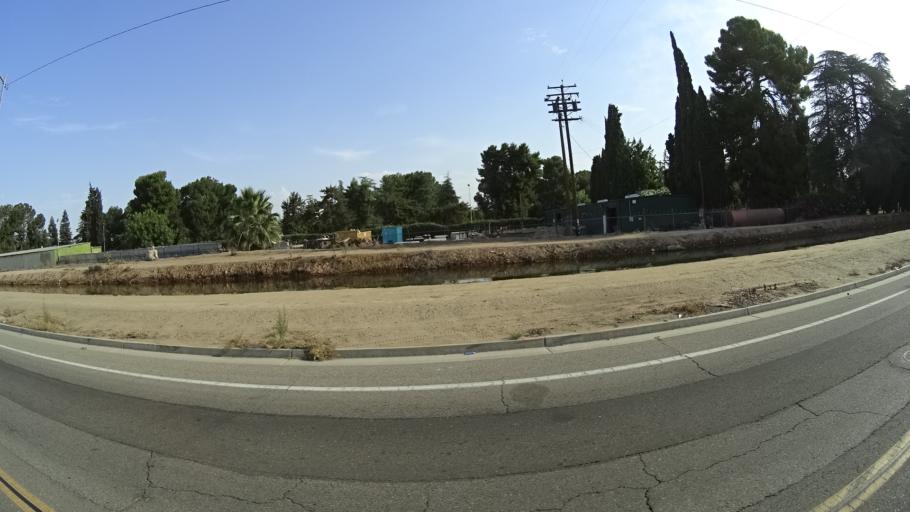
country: US
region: California
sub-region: Fresno County
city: West Park
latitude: 36.7430
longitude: -119.8288
